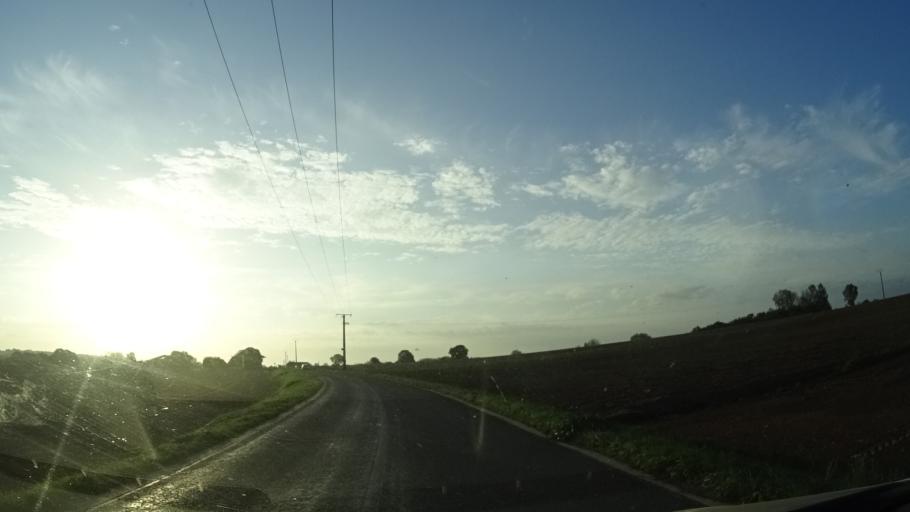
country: BE
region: Wallonia
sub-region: Province du Hainaut
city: Beaumont
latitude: 50.2657
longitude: 4.2227
